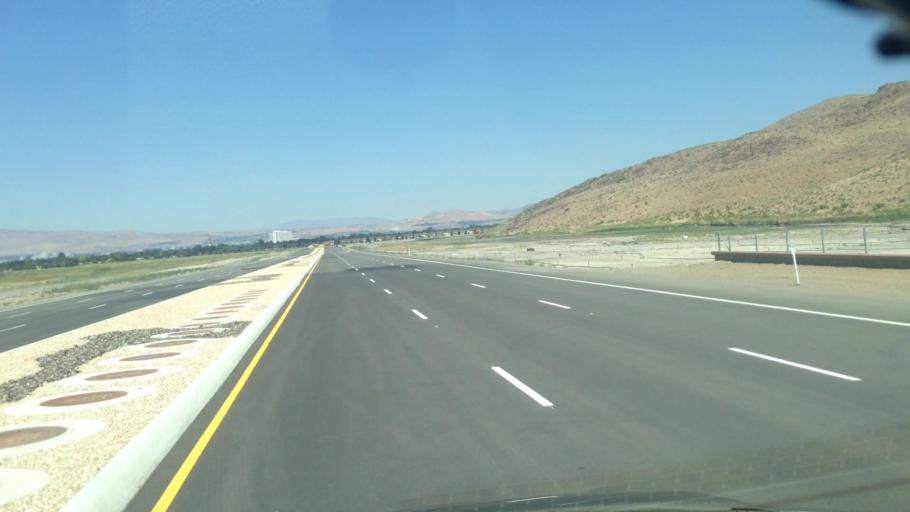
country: US
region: Nevada
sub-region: Washoe County
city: Sparks
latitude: 39.4688
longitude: -119.7317
